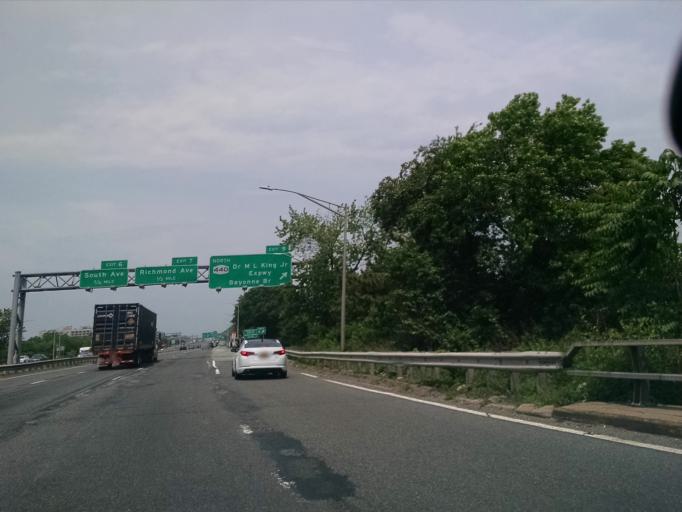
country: US
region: New York
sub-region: Richmond County
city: Bloomfield
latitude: 40.6096
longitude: -74.1501
